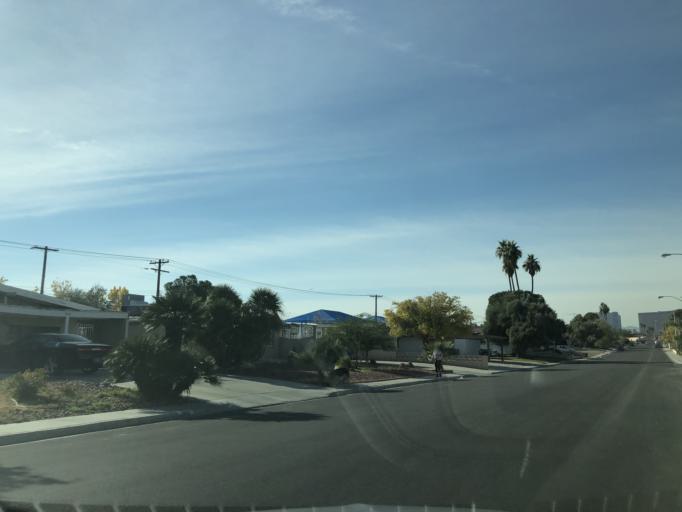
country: US
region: Nevada
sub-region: Clark County
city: Winchester
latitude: 36.1264
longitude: -115.1290
